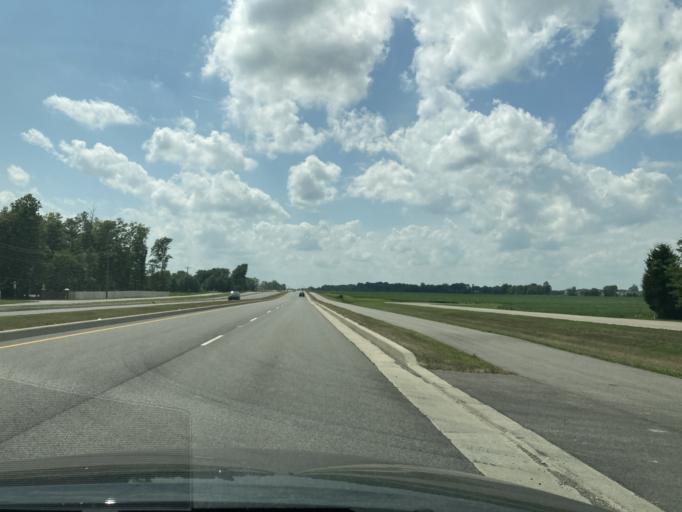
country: US
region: Indiana
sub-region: Hamilton County
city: Carmel
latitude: 39.9996
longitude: -86.1906
